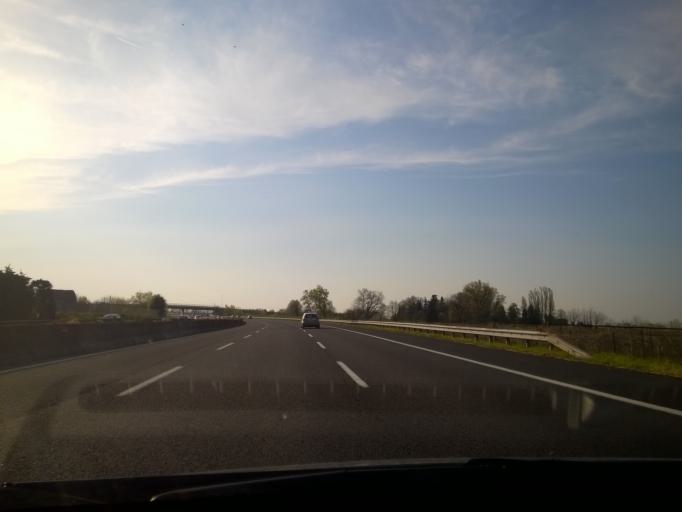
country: IT
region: Emilia-Romagna
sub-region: Provincia di Ravenna
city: Solarolo
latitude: 44.3375
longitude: 11.8707
